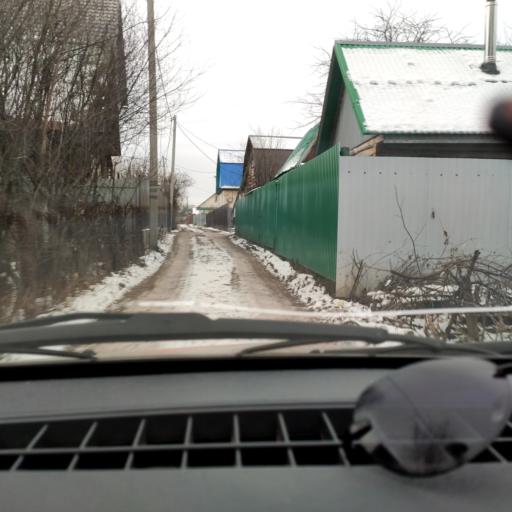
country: RU
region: Bashkortostan
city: Ufa
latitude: 54.7737
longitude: 55.9343
